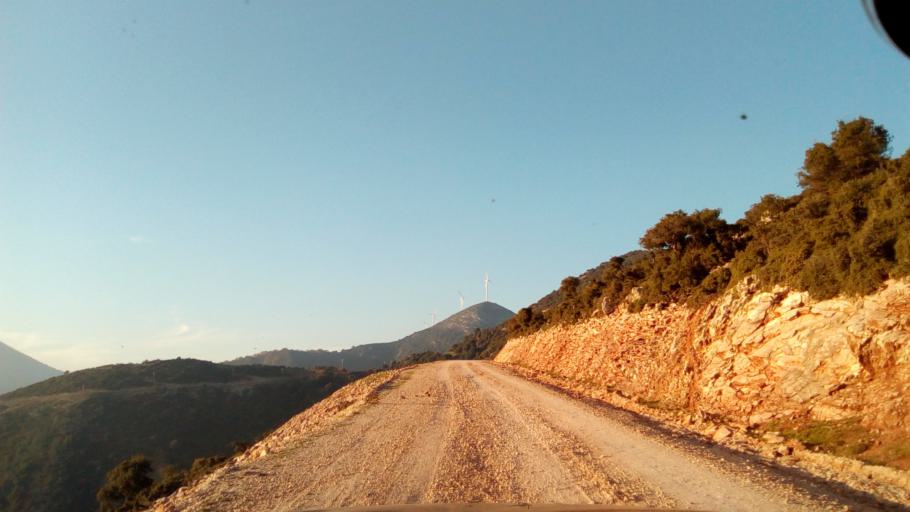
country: GR
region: West Greece
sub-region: Nomos Aitolias kai Akarnanias
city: Nafpaktos
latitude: 38.4355
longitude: 21.8488
